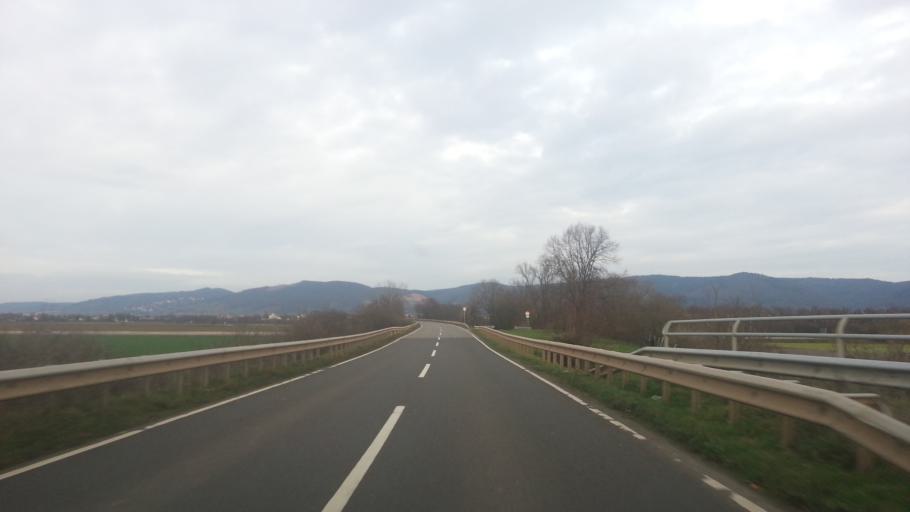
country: DE
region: Baden-Wuerttemberg
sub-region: Karlsruhe Region
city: Eppelheim
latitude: 49.4185
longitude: 8.6257
